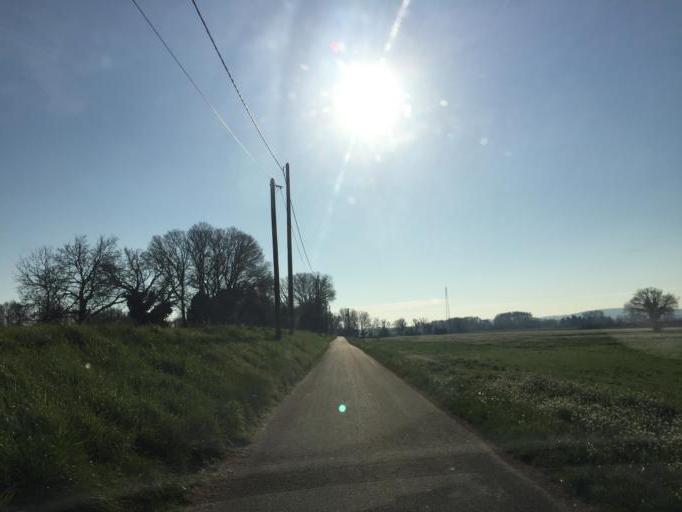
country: FR
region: Provence-Alpes-Cote d'Azur
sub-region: Departement du Vaucluse
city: Bedarrides
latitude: 44.0577
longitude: 4.9283
